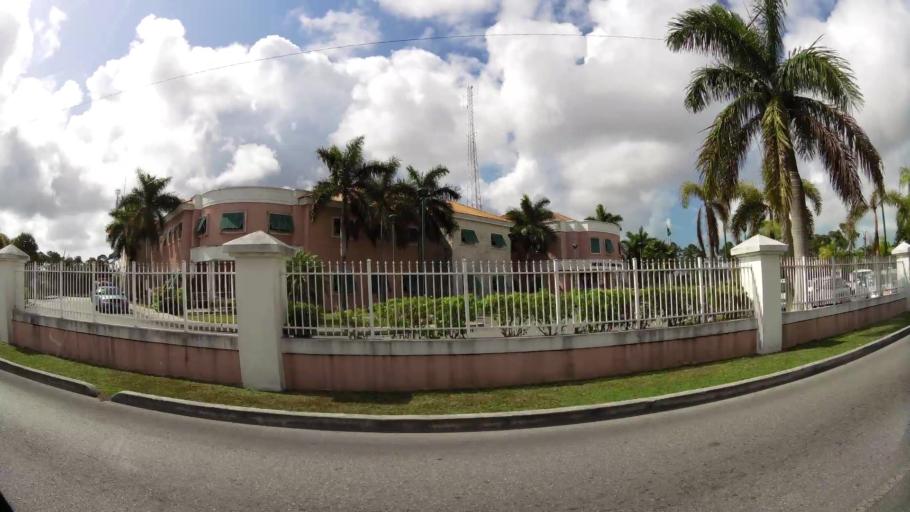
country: BS
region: Freeport
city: Freeport
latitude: 26.5366
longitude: -78.6959
